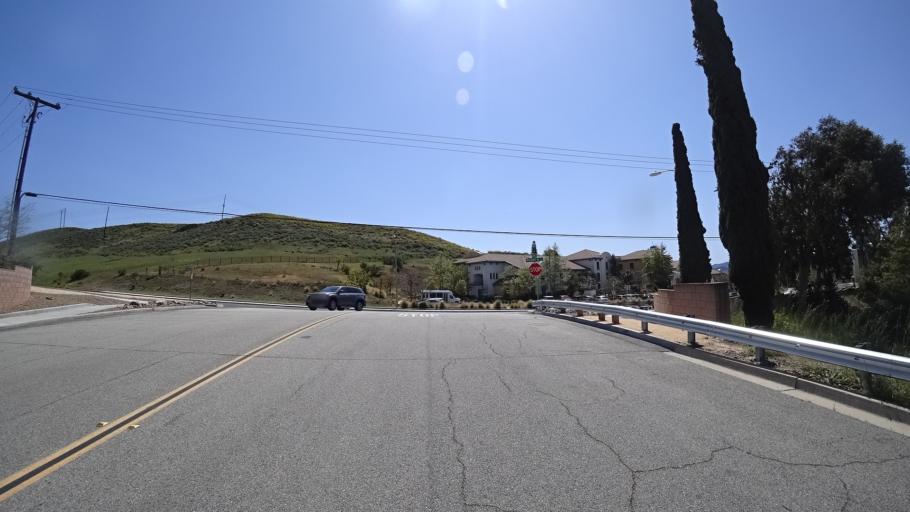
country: US
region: California
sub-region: Ventura County
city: Moorpark
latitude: 34.2310
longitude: -118.8713
